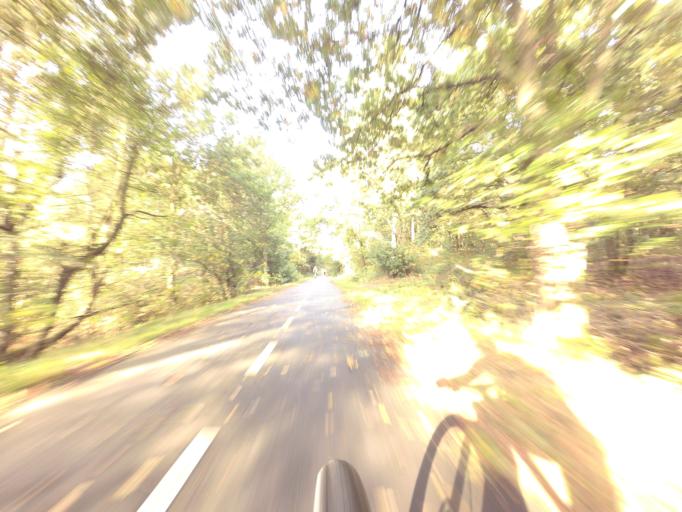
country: DK
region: Central Jutland
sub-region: Viborg Kommune
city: Viborg
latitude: 56.4232
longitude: 9.4345
